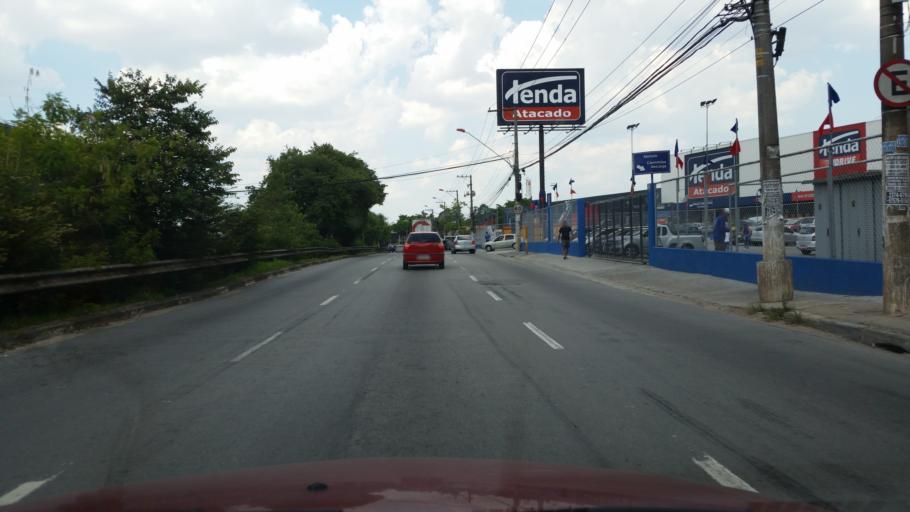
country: BR
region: Sao Paulo
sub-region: Diadema
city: Diadema
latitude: -23.6810
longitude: -46.5982
